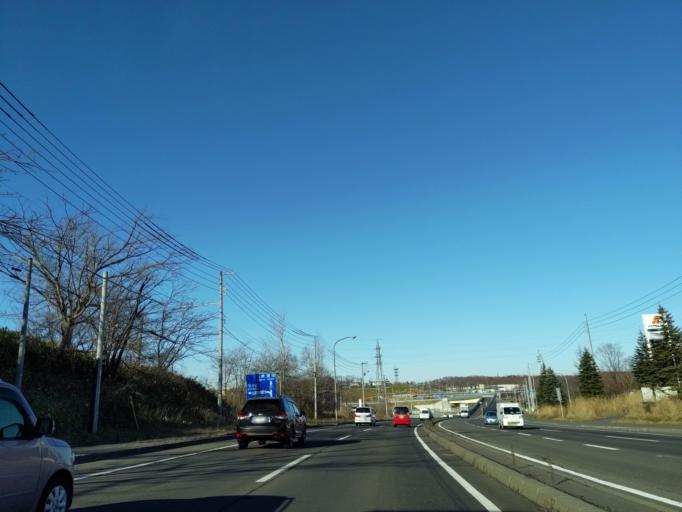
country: JP
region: Hokkaido
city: Kitahiroshima
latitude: 42.9527
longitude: 141.4962
